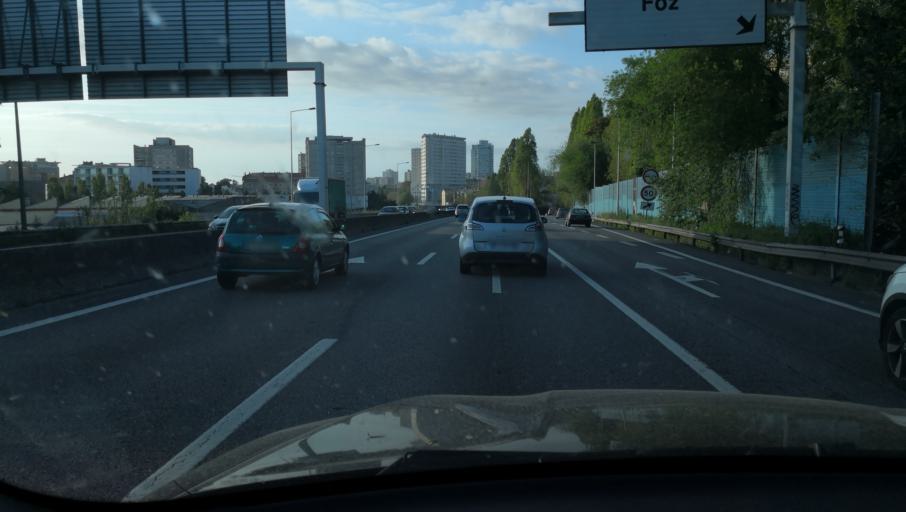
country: PT
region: Porto
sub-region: Vila Nova de Gaia
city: Canidelo
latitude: 41.1544
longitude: -8.6450
